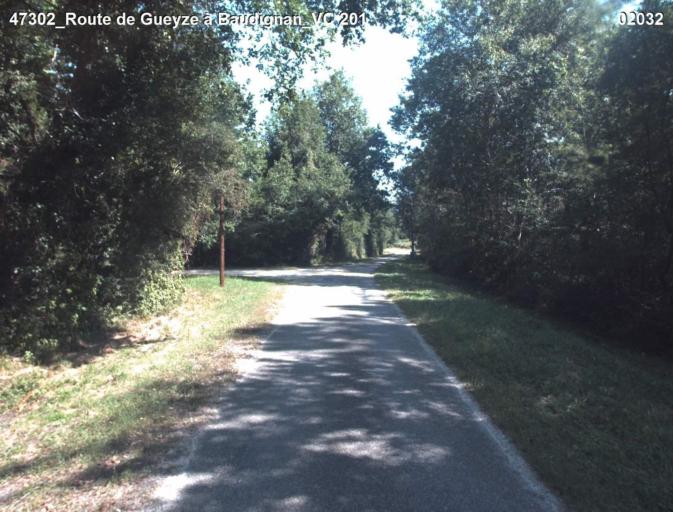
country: FR
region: Aquitaine
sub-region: Departement des Landes
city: Gabarret
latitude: 44.0559
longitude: 0.1139
